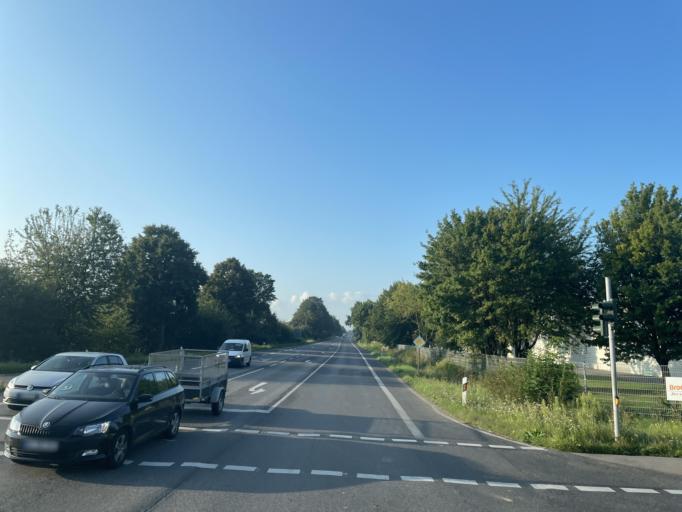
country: DE
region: North Rhine-Westphalia
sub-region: Regierungsbezirk Dusseldorf
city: Neubrueck
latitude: 51.1675
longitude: 6.5935
